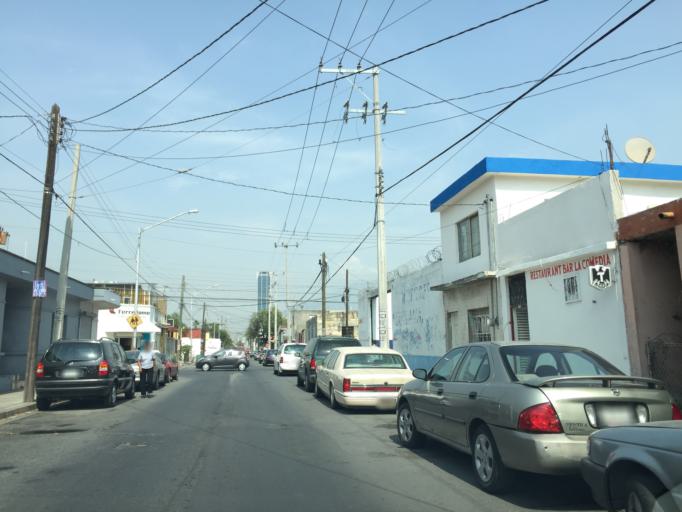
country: MX
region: Nuevo Leon
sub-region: Monterrey
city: Monterrey
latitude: 25.6617
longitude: -100.3015
